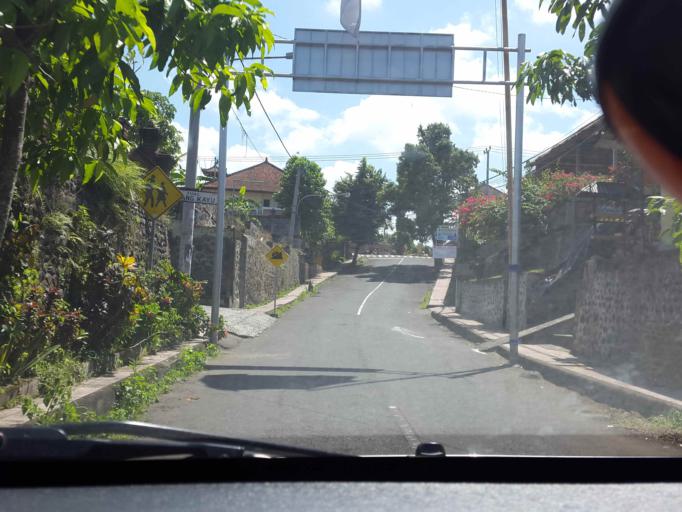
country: ID
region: Bali
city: Klungkung
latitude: -8.5349
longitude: 115.3947
